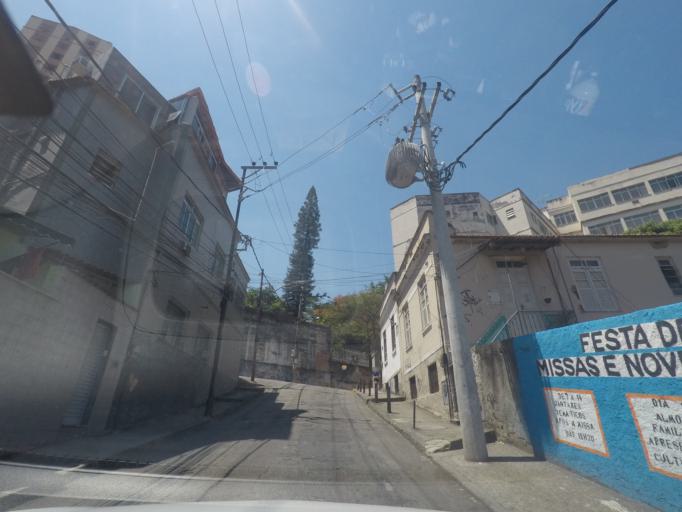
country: BR
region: Rio de Janeiro
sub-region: Rio De Janeiro
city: Rio de Janeiro
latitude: -22.9032
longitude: -43.2222
